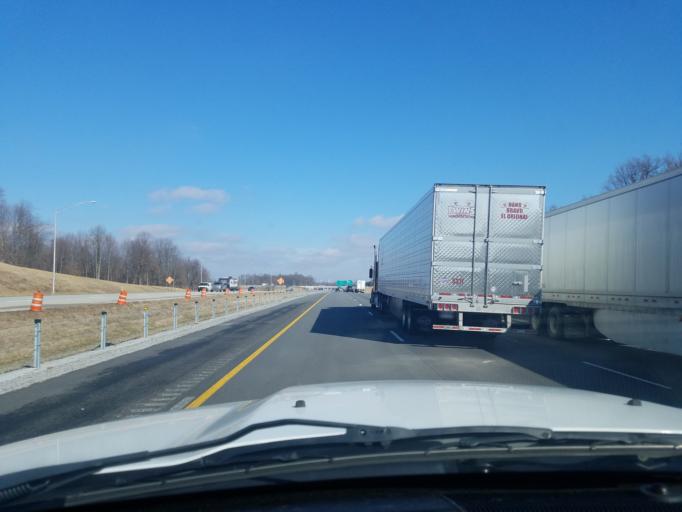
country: US
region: Kentucky
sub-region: Hardin County
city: Elizabethtown
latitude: 37.6957
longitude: -85.8381
